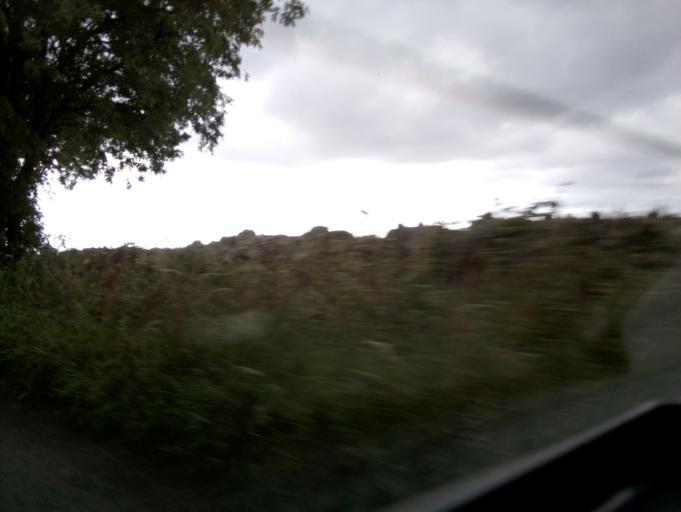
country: GB
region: England
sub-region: Gloucestershire
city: Shurdington
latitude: 51.7974
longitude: -2.1235
